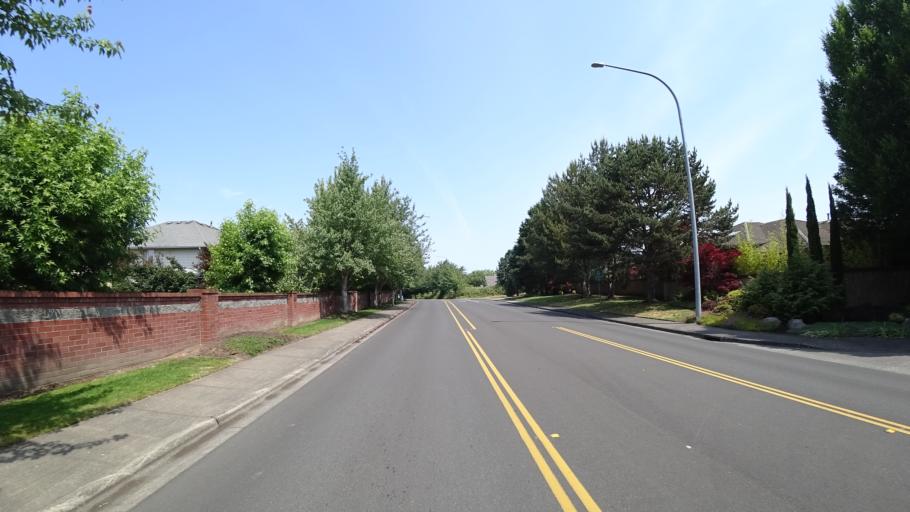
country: US
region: Oregon
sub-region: Washington County
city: Oak Hills
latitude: 45.5436
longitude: -122.8246
